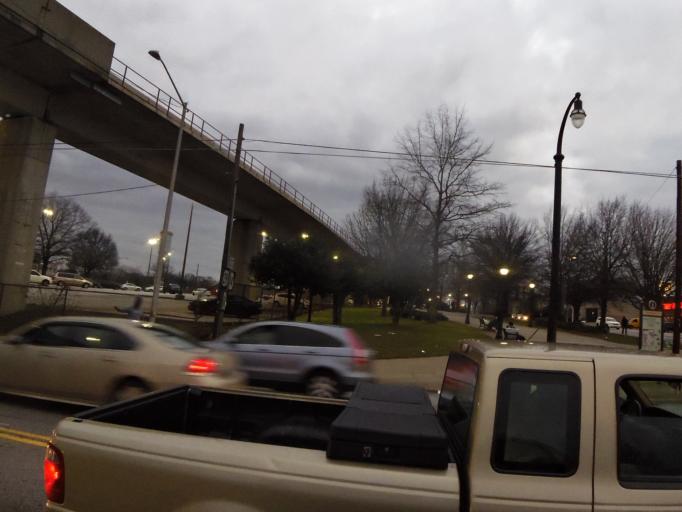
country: US
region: Georgia
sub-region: Fulton County
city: Atlanta
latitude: 33.7382
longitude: -84.4137
